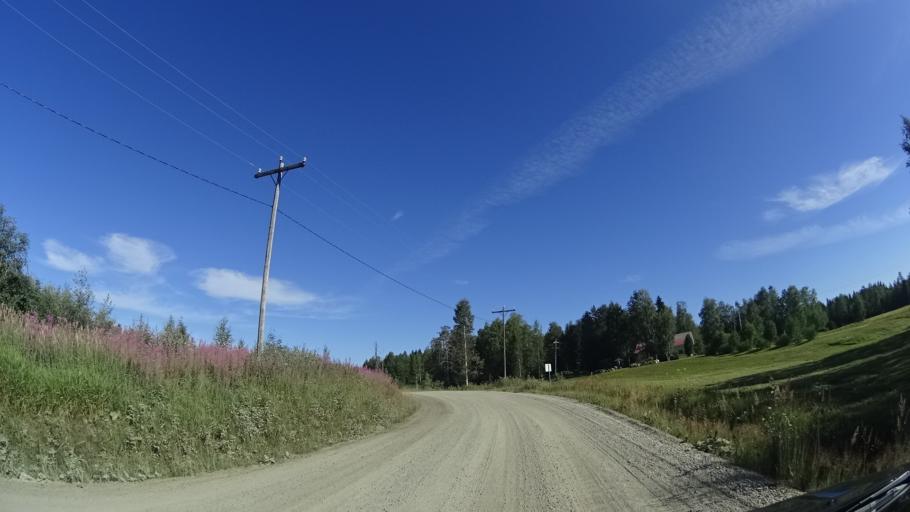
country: FI
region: Central Finland
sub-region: Jyvaeskylae
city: Petaejaevesi
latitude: 62.3507
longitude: 25.3310
